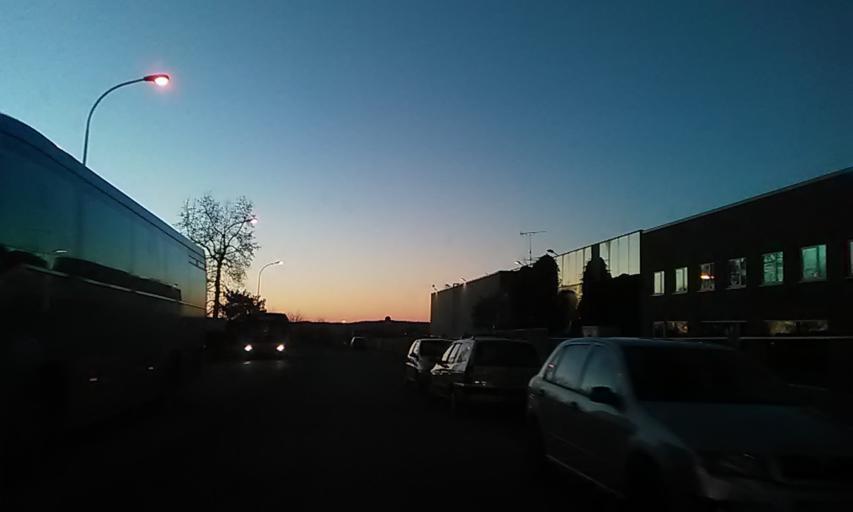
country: IT
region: Piedmont
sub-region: Provincia di Biella
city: Occhieppo Inferiore
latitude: 45.5543
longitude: 8.0317
